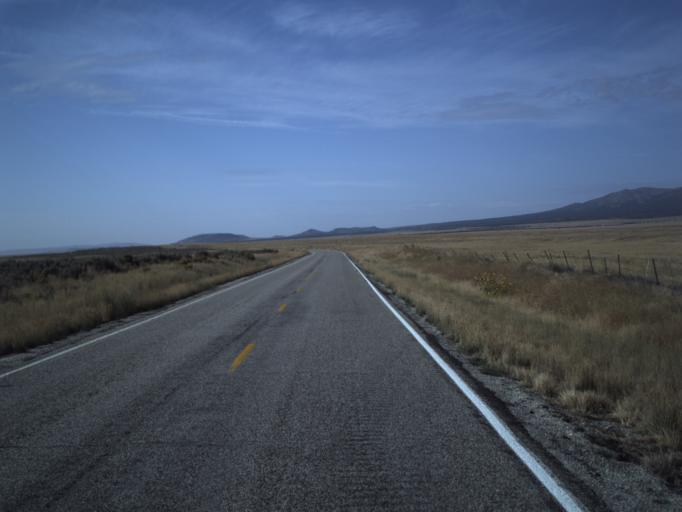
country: US
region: Idaho
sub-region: Oneida County
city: Malad City
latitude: 41.9520
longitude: -113.0759
